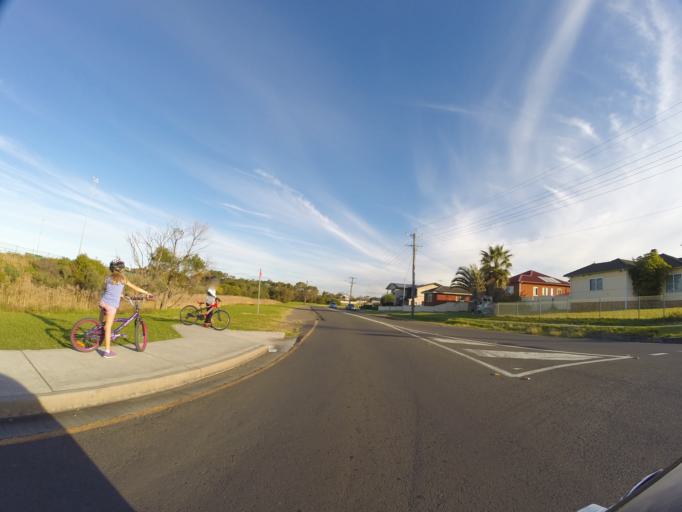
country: AU
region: New South Wales
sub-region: Wollongong
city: Bulli
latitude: -34.3446
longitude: 150.9197
